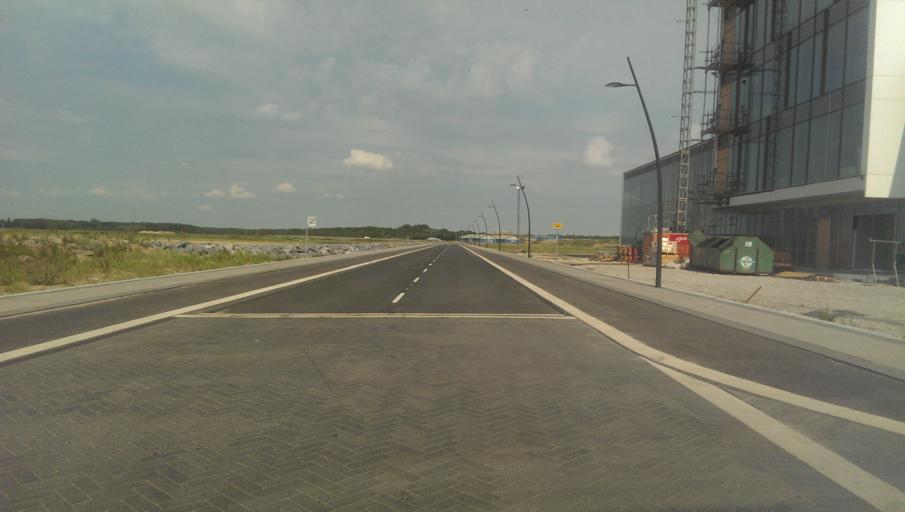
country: DK
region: South Denmark
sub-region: Fano Kommune
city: Nordby
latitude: 55.4811
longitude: 8.4117
